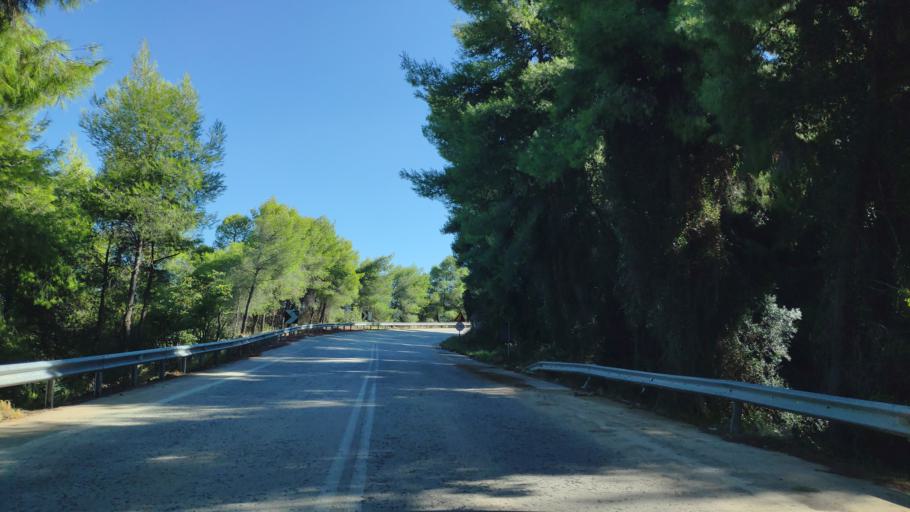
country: GR
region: Peloponnese
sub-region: Nomos Korinthias
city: Loutra Oraias Elenis
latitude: 37.8337
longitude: 23.0242
